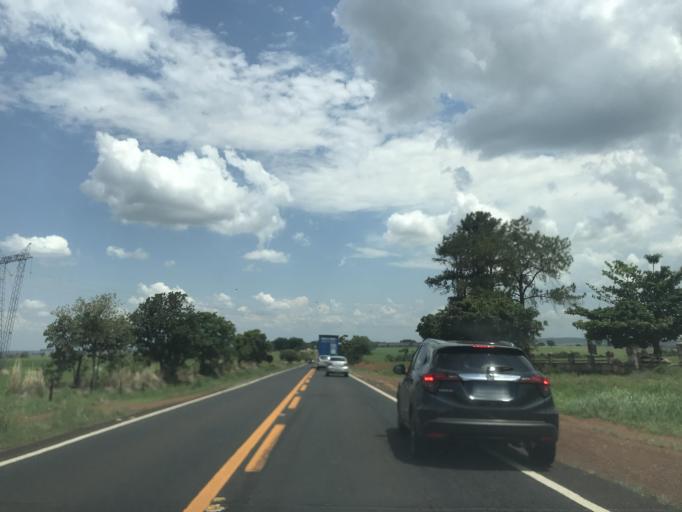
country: BR
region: Goias
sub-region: Piracanjuba
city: Piracanjuba
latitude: -17.4626
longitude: -48.7626
